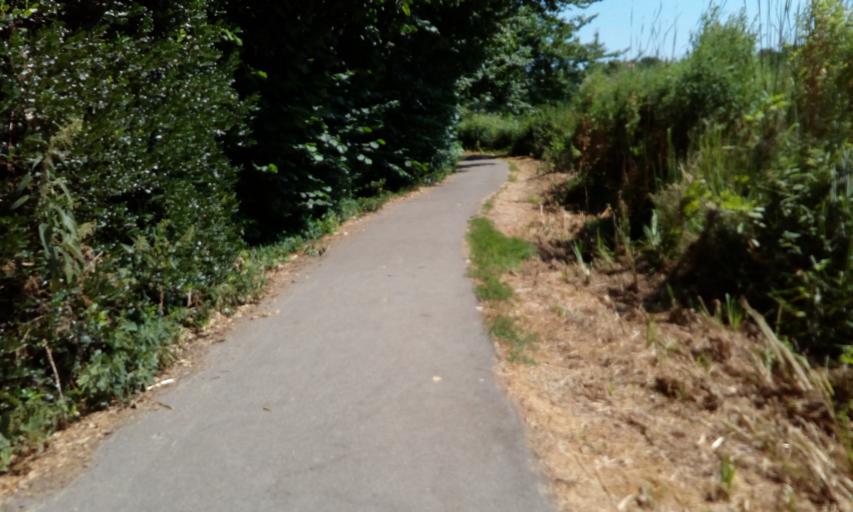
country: NL
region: South Holland
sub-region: Gemeente Capelle aan den IJssel
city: Capelle aan den IJssel
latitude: 51.9451
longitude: 4.5777
